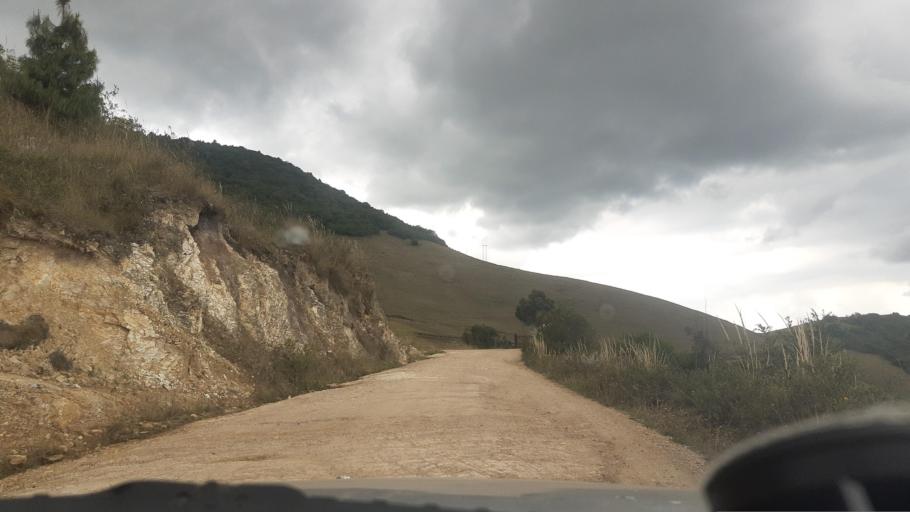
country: CO
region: Cundinamarca
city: Suesca
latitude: 5.1588
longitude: -73.8010
